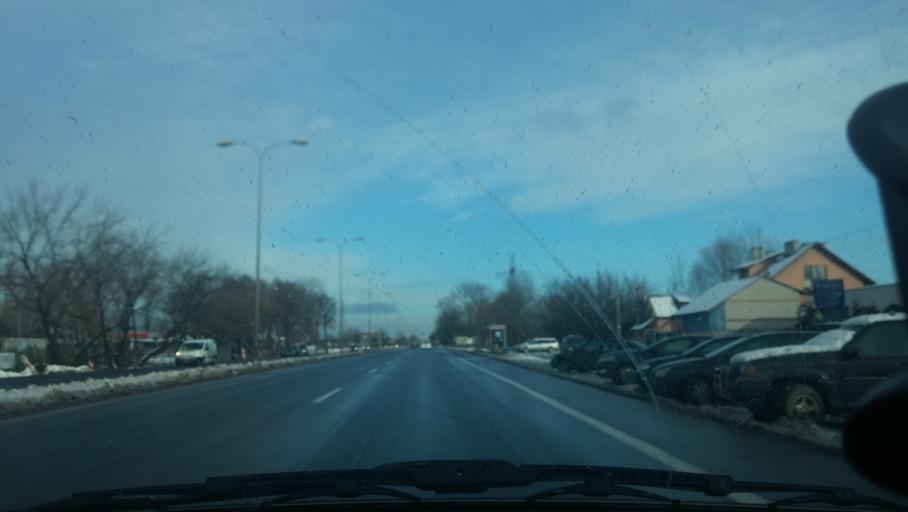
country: PL
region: Masovian Voivodeship
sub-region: Powiat wolominski
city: Zabki
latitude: 52.2909
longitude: 21.0788
